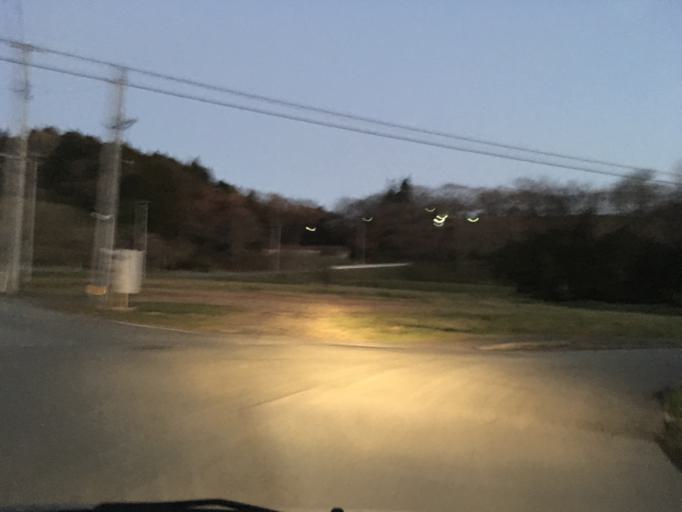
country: JP
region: Iwate
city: Ichinoseki
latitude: 38.8512
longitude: 141.2930
